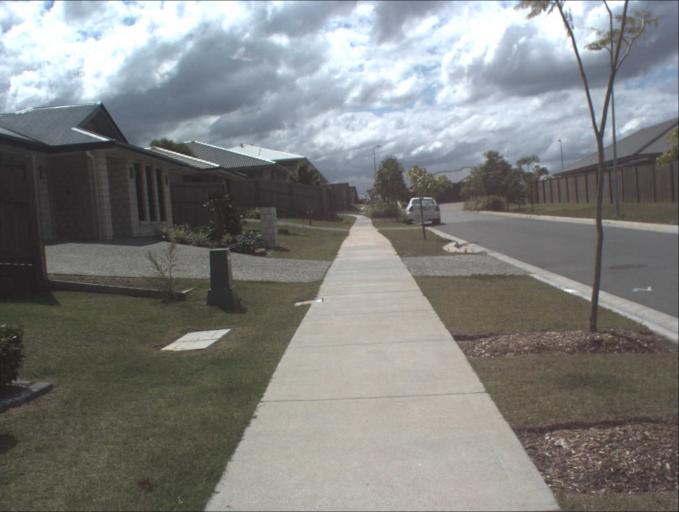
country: AU
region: Queensland
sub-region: Logan
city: Chambers Flat
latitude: -27.8019
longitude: 153.1095
